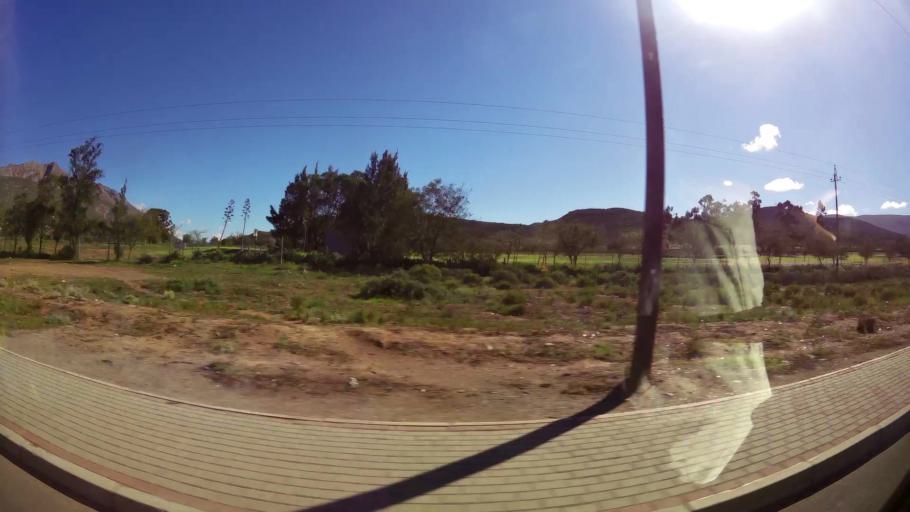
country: ZA
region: Western Cape
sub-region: Cape Winelands District Municipality
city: Ashton
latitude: -33.7717
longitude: 20.1384
